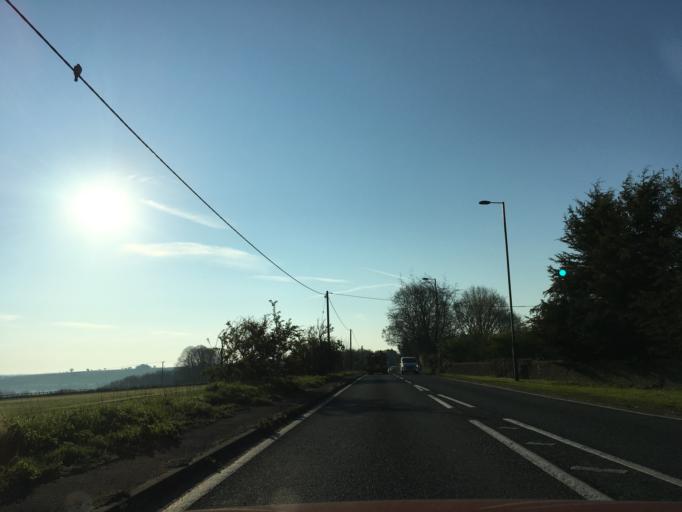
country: GB
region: England
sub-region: Oxfordshire
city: Burford
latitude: 51.8013
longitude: -1.6315
